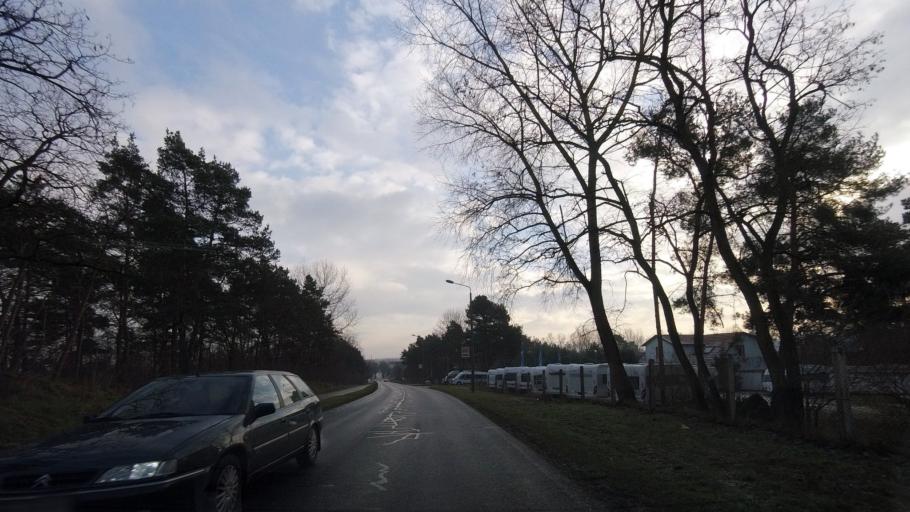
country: DE
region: Brandenburg
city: Luckenwalde
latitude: 52.0965
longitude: 13.1478
